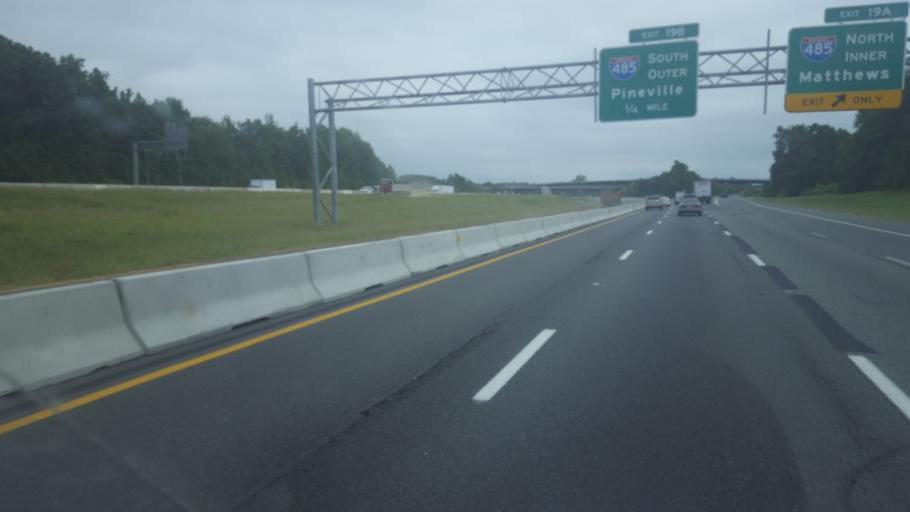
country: US
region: North Carolina
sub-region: Mecklenburg County
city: Huntersville
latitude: 35.3579
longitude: -80.8433
